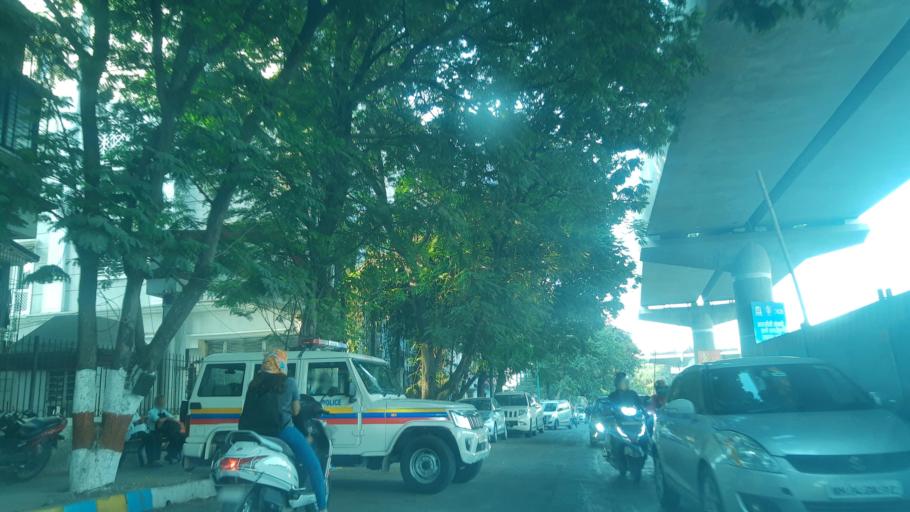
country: IN
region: Maharashtra
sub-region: Thane
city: Thane
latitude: 19.1984
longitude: 72.9626
